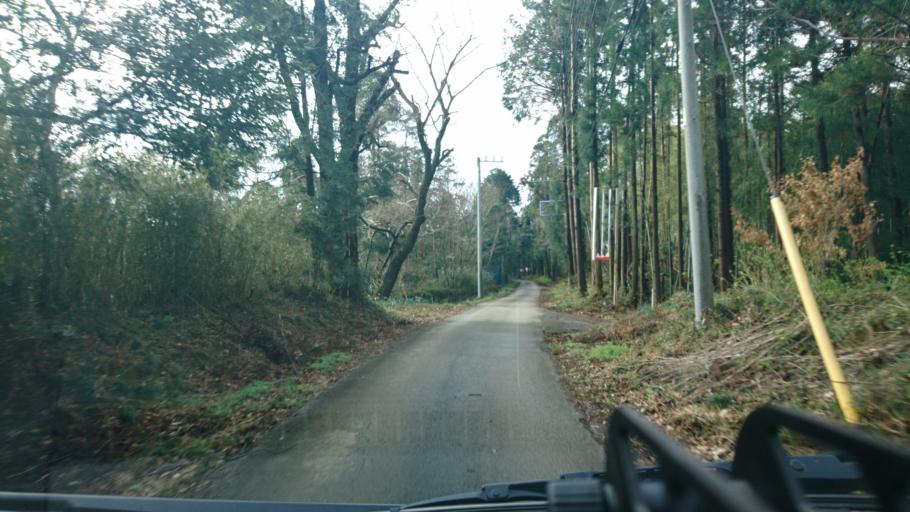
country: JP
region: Chiba
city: Kisarazu
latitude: 35.3306
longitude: 139.9649
